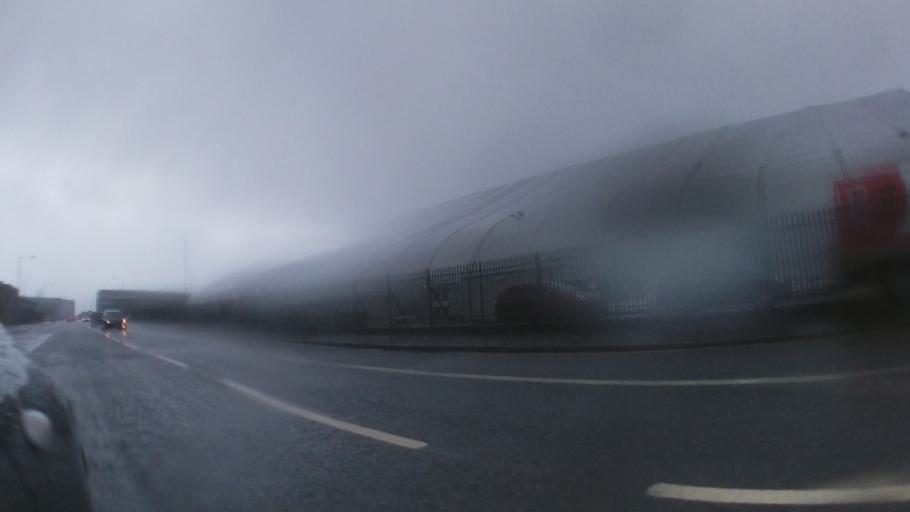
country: GB
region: Northern Ireland
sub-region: City of Belfast
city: Belfast
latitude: 54.6103
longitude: -5.9048
